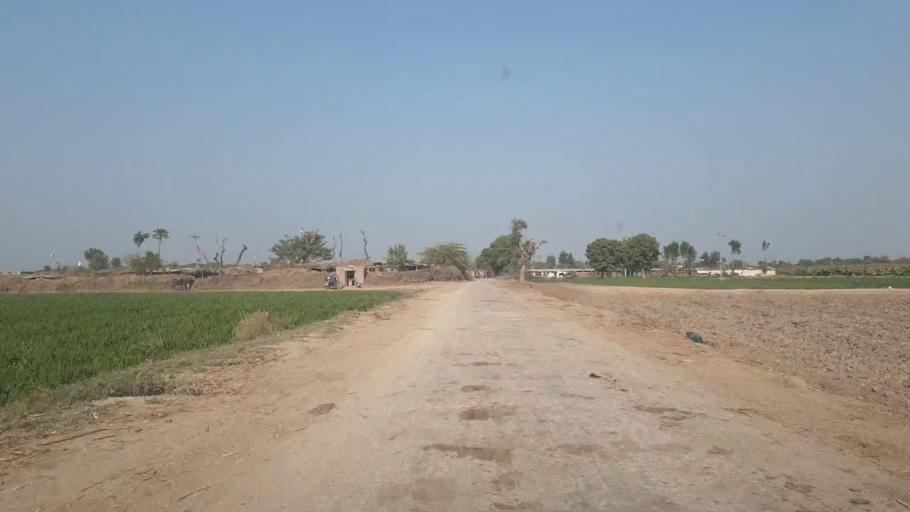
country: PK
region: Sindh
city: Tando Allahyar
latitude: 25.4475
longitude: 68.7887
